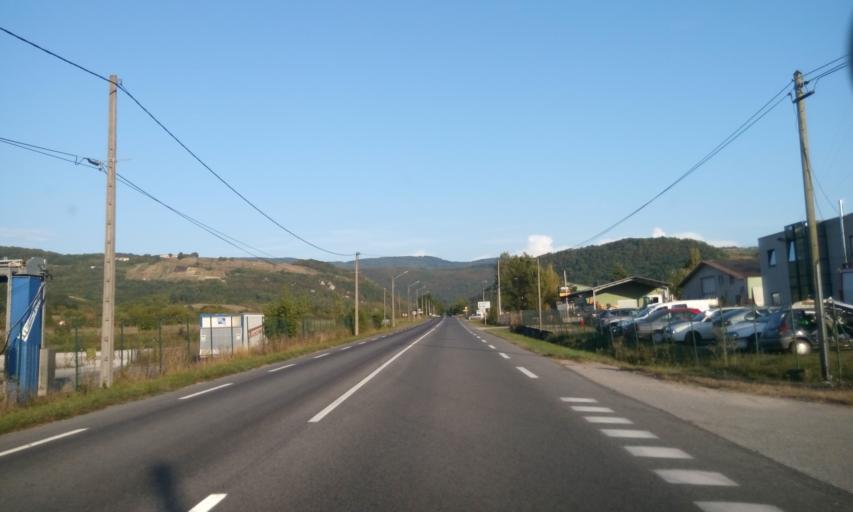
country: FR
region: Rhone-Alpes
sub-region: Departement de l'Ain
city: Poncin
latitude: 46.0814
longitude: 5.4126
